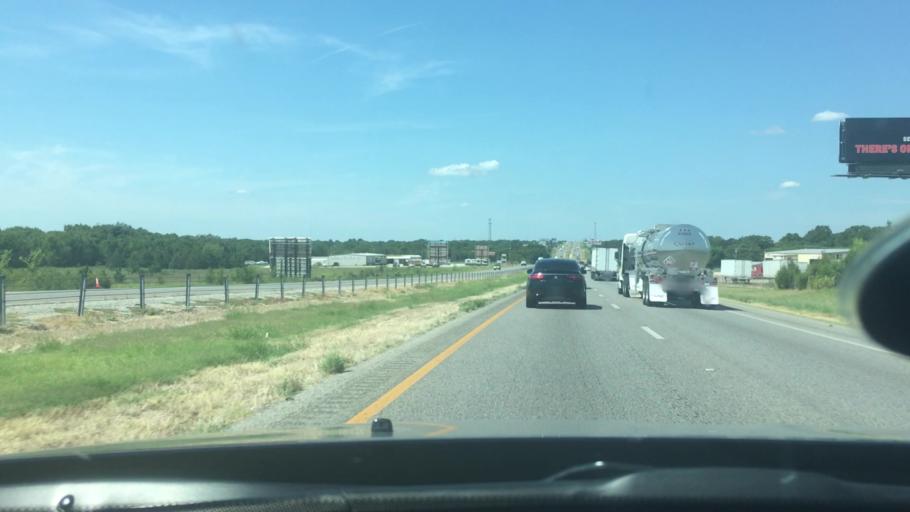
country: US
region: Oklahoma
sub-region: Bryan County
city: Calera
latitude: 33.9257
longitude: -96.4355
